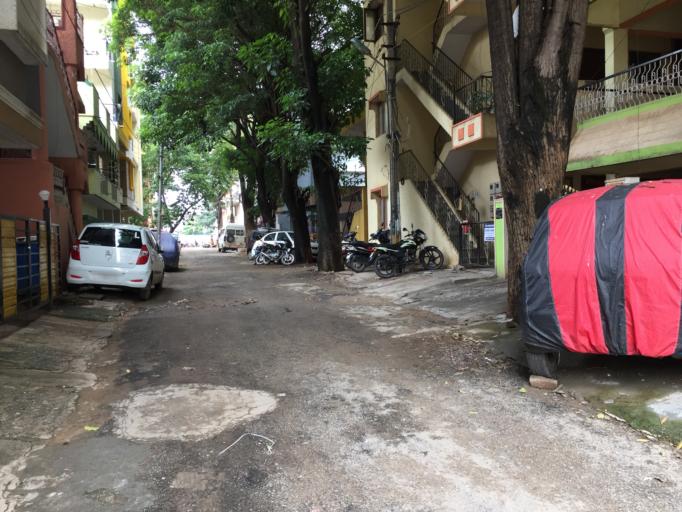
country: IN
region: Karnataka
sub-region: Bangalore Urban
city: Bangalore
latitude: 12.9556
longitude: 77.6544
